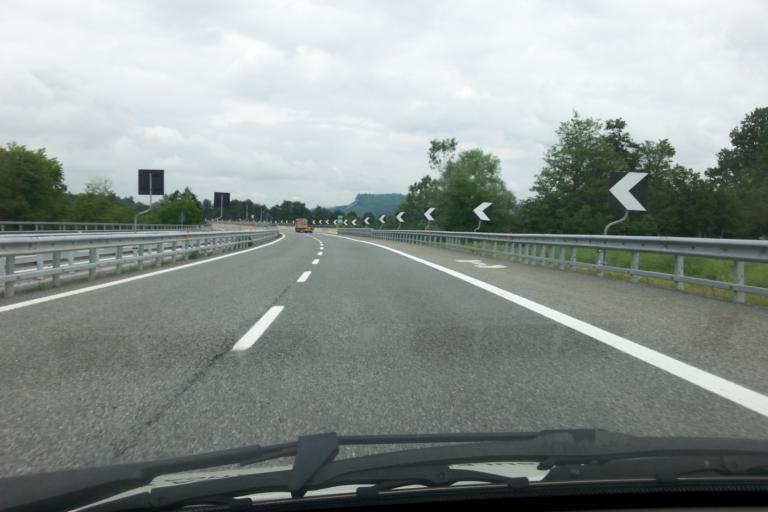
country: IT
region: Piedmont
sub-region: Provincia di Cuneo
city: Lesegno
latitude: 44.4099
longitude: 7.9659
